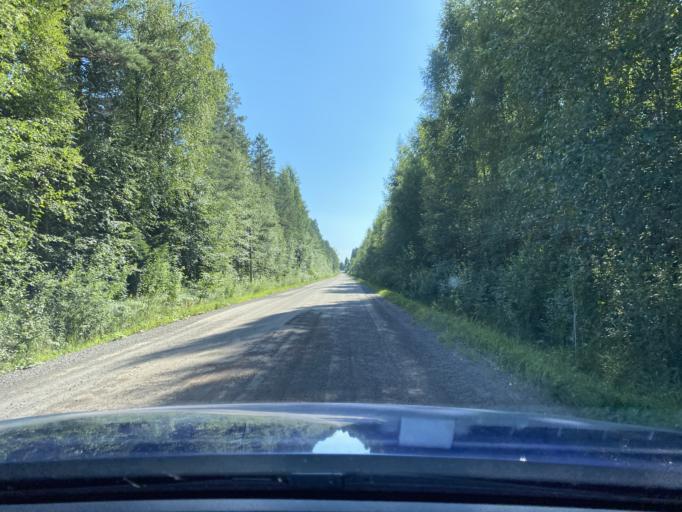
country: FI
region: Satakunta
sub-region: Rauma
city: Kiukainen
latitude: 61.1431
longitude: 21.9969
